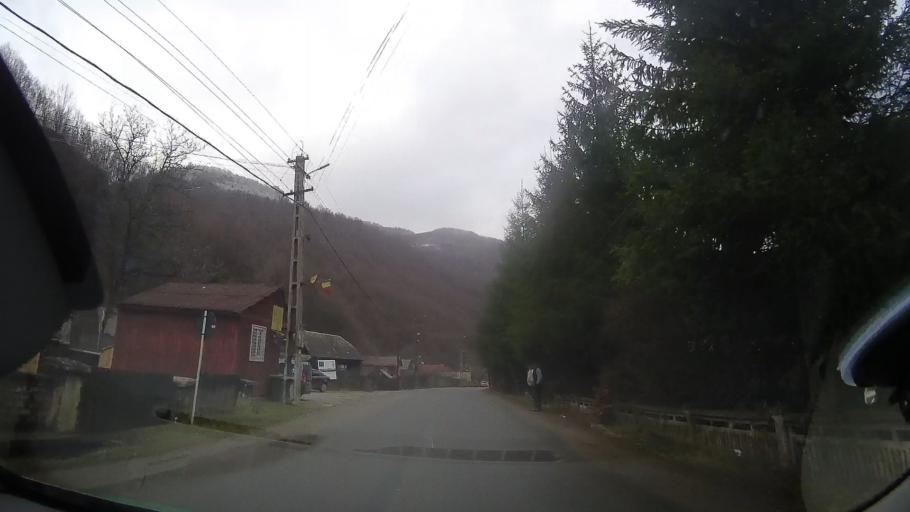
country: RO
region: Cluj
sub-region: Comuna Maguri-Racatau
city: Maguri-Racatau
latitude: 46.6483
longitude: 23.1969
